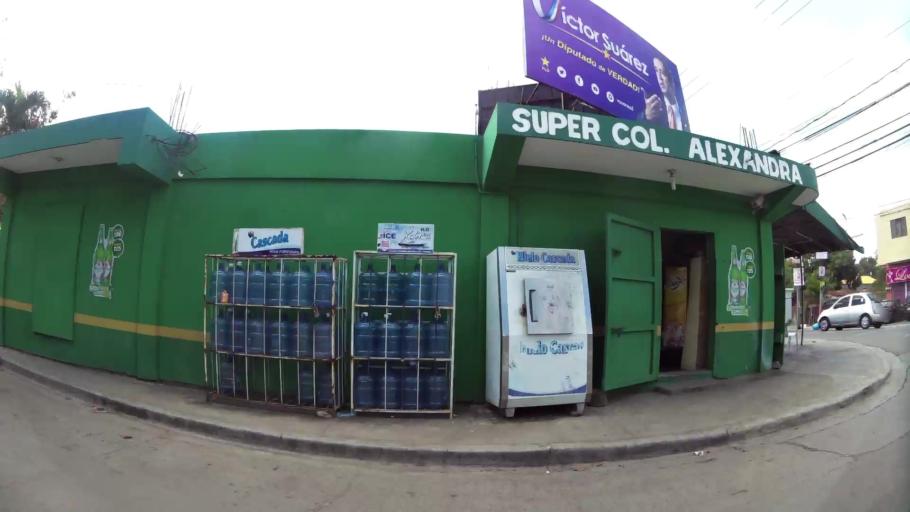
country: DO
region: Santiago
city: Santiago de los Caballeros
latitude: 19.4768
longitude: -70.6694
